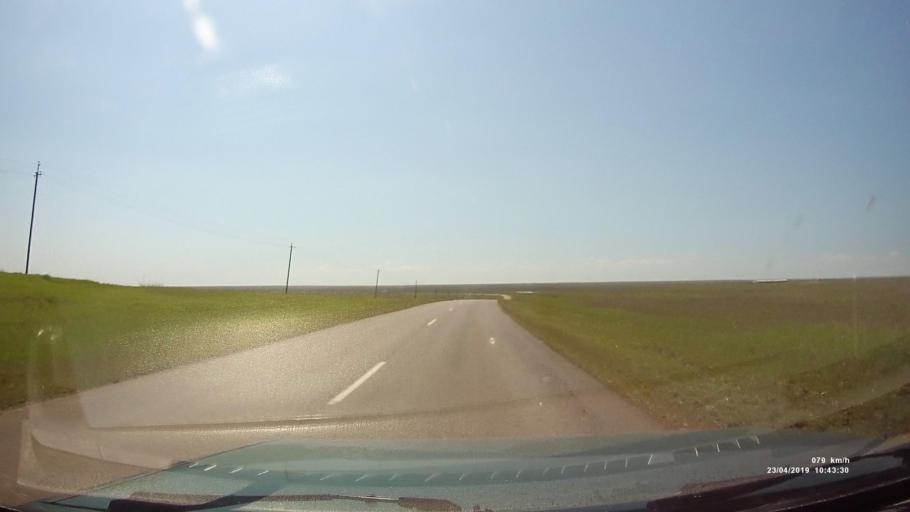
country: RU
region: Kalmykiya
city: Yashalta
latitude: 46.4695
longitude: 42.6499
